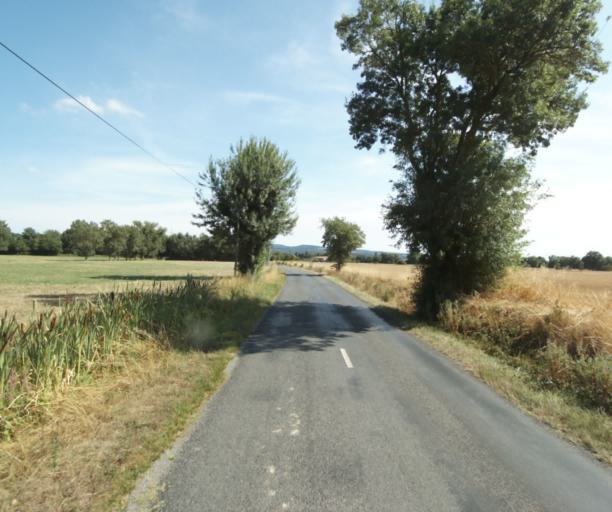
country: FR
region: Midi-Pyrenees
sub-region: Departement de la Haute-Garonne
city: Revel
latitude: 43.4819
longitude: 1.9883
